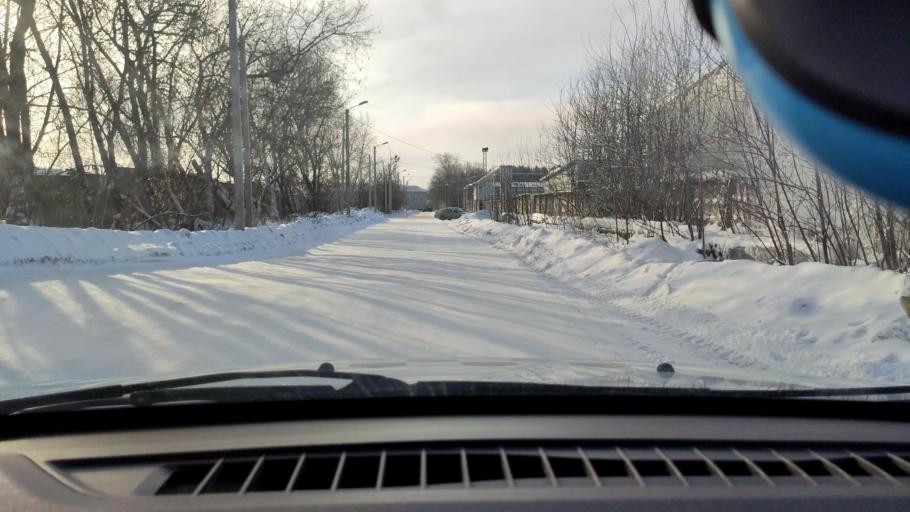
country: RU
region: Perm
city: Kultayevo
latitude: 57.9953
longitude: 55.9250
